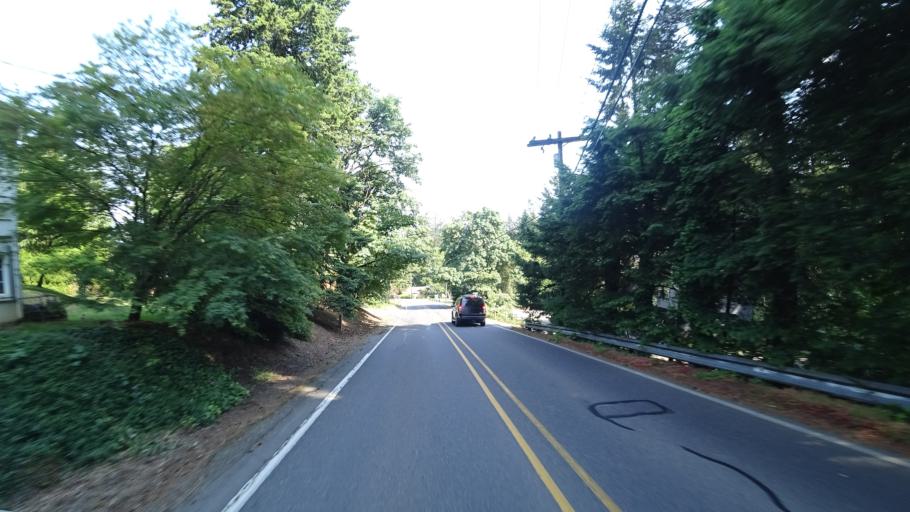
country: US
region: Oregon
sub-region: Clackamas County
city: Happy Valley
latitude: 45.4517
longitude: -122.5382
